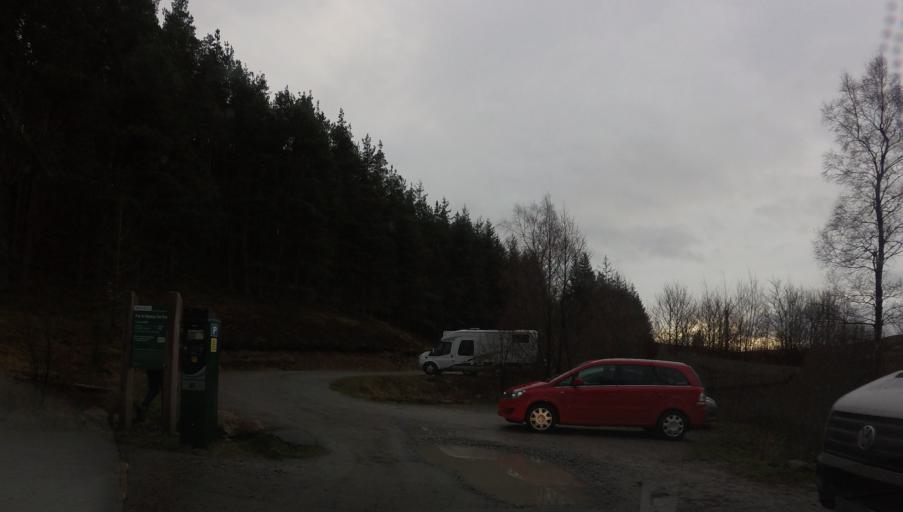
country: GB
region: Scotland
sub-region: Perth and Kinross
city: Aberfeldy
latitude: 56.6761
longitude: -4.0362
